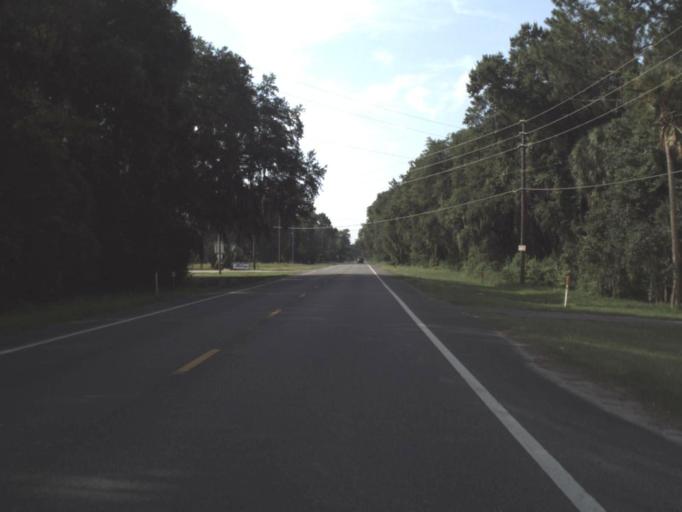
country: US
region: Florida
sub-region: Taylor County
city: Perry
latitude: 30.1430
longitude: -83.5877
